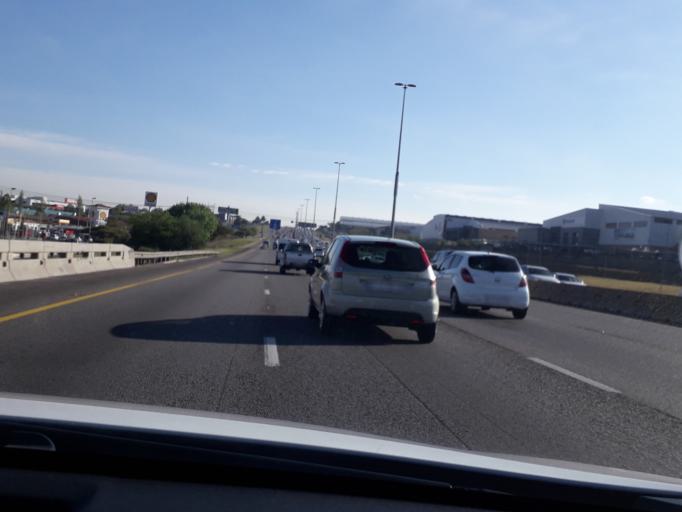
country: ZA
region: Gauteng
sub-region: City of Johannesburg Metropolitan Municipality
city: Midrand
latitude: -25.9288
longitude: 28.1449
